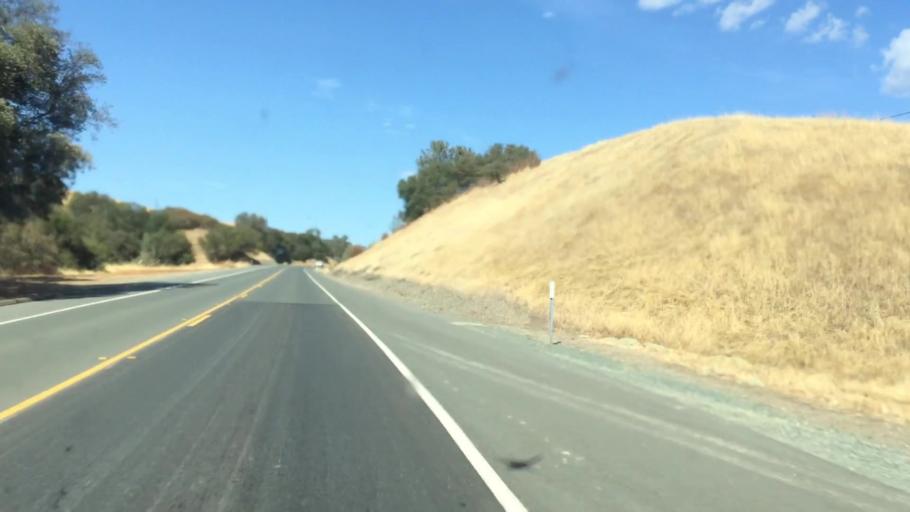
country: US
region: California
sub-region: Amador County
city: Ione
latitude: 38.3703
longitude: -120.9196
